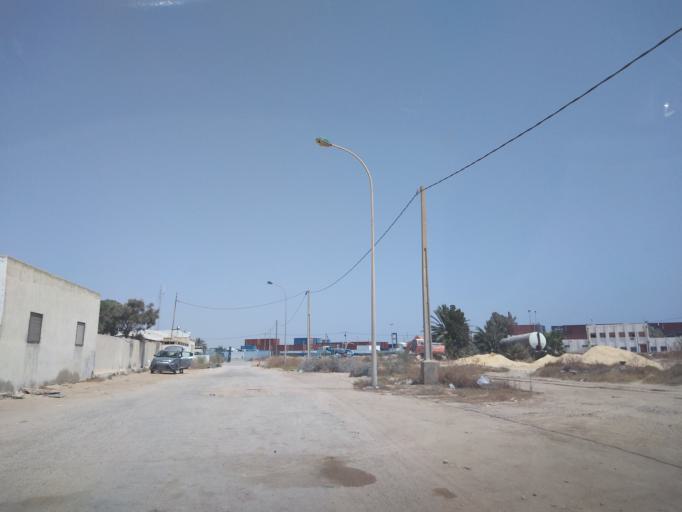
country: TN
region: Safaqis
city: Al Qarmadah
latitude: 34.7275
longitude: 10.7796
